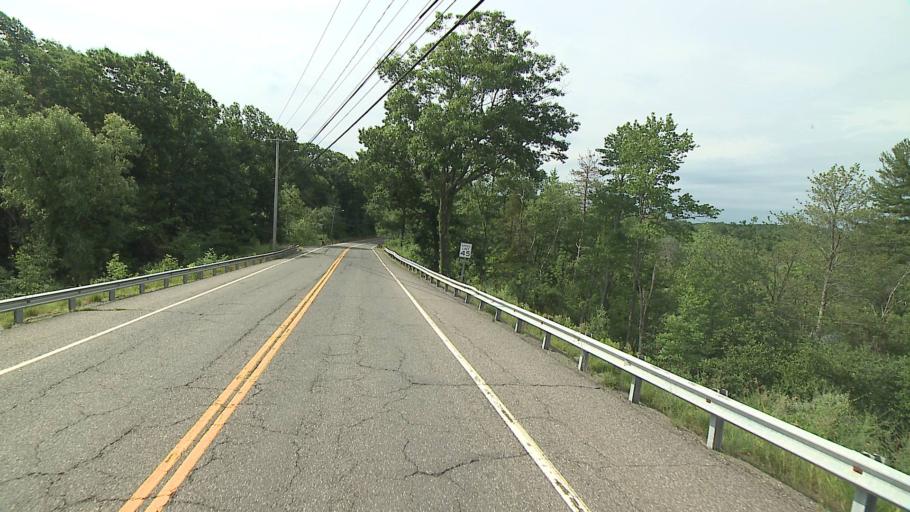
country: US
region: Connecticut
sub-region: Litchfield County
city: Torrington
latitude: 41.8492
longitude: -73.0973
